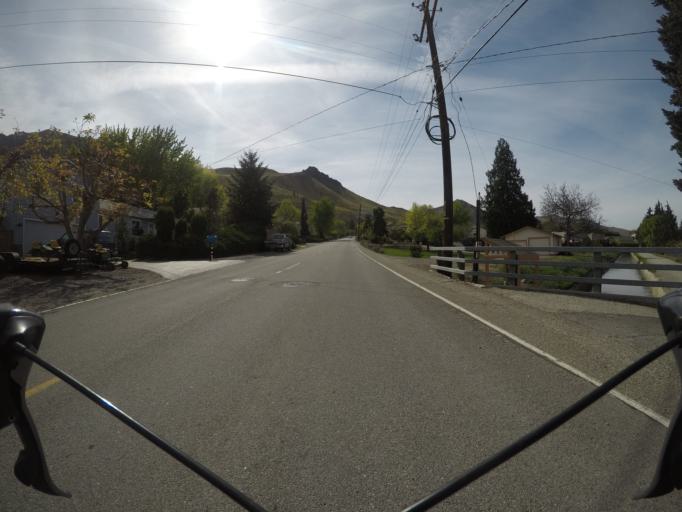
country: US
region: Washington
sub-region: Chelan County
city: Wenatchee
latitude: 47.4080
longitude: -120.3325
